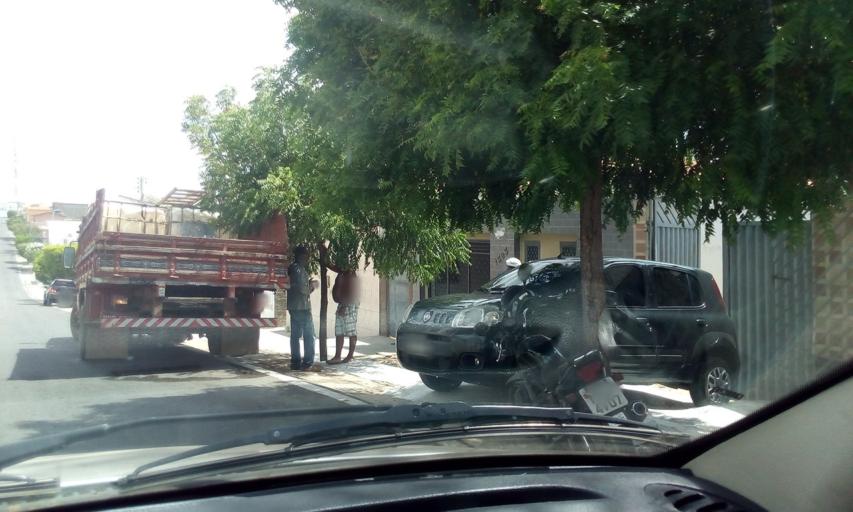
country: BR
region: Rio Grande do Norte
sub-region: Currais Novos
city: Currais Novos
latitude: -6.2655
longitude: -36.5199
